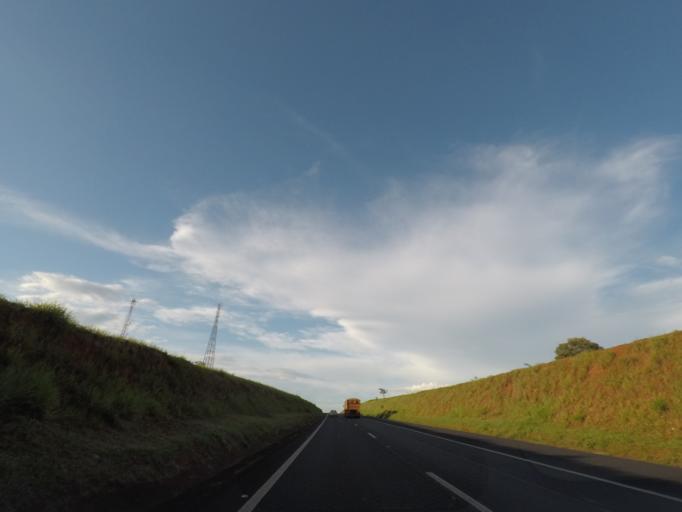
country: BR
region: Sao Paulo
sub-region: Ituverava
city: Ituverava
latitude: -20.2724
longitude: -47.7979
